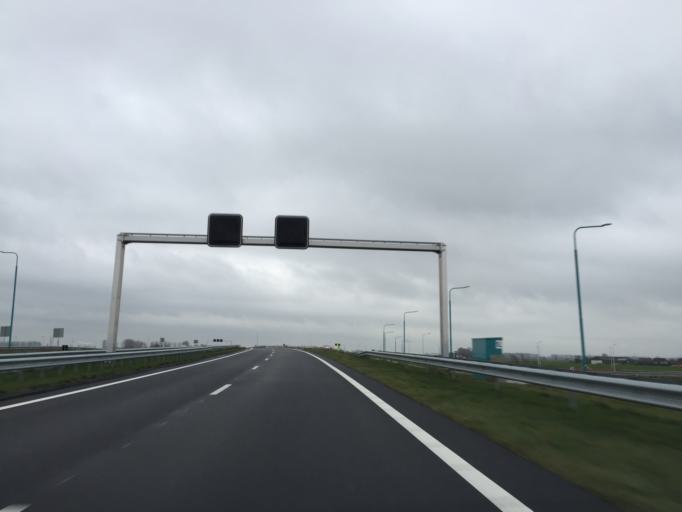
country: NL
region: Zeeland
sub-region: Gemeente Terneuzen
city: Sluiskil
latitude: 51.2981
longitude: 3.8063
